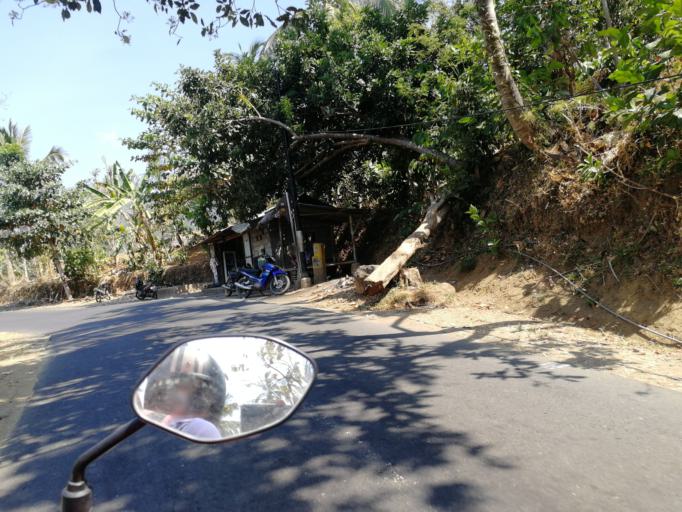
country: ID
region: Bali
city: Banjar Kedisan
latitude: -8.1407
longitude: 115.3156
